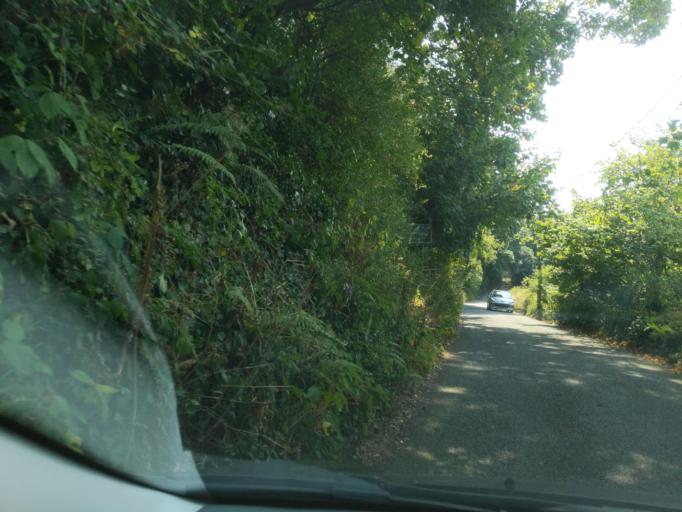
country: GB
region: England
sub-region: Cornwall
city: Fowey
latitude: 50.3423
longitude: -4.6293
